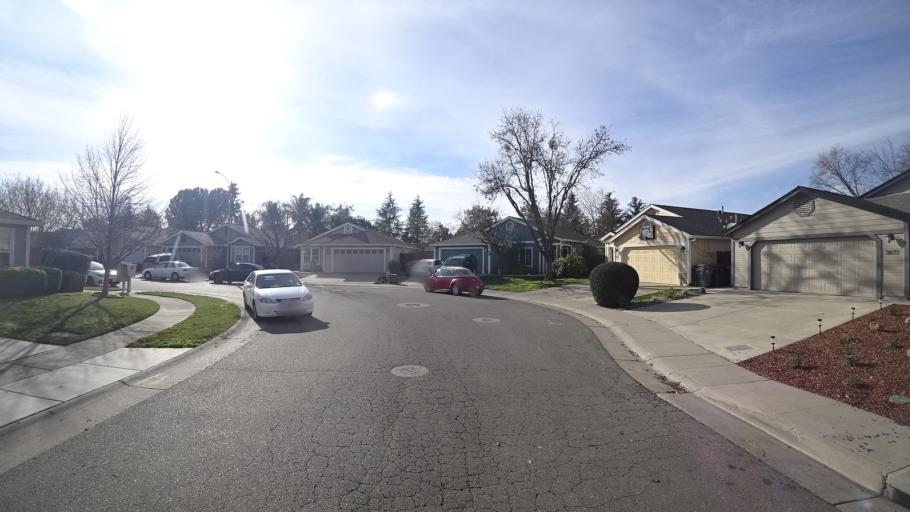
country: US
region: California
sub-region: Yolo County
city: Davis
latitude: 38.5491
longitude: -121.7066
